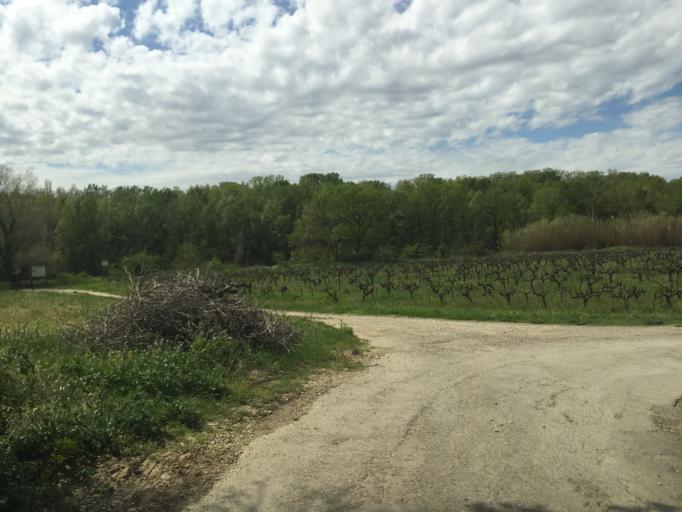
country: FR
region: Provence-Alpes-Cote d'Azur
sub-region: Departement du Vaucluse
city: Chateauneuf-du-Pape
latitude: 44.0490
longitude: 4.8132
